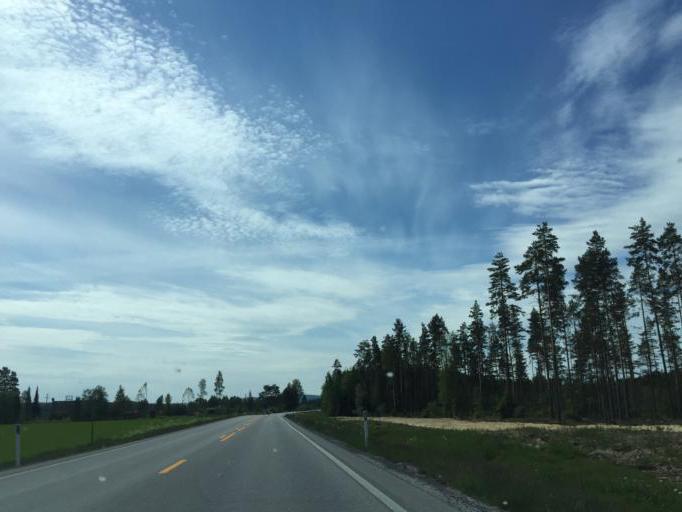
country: NO
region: Hedmark
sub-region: Sor-Odal
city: Skarnes
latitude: 60.2326
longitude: 11.6673
